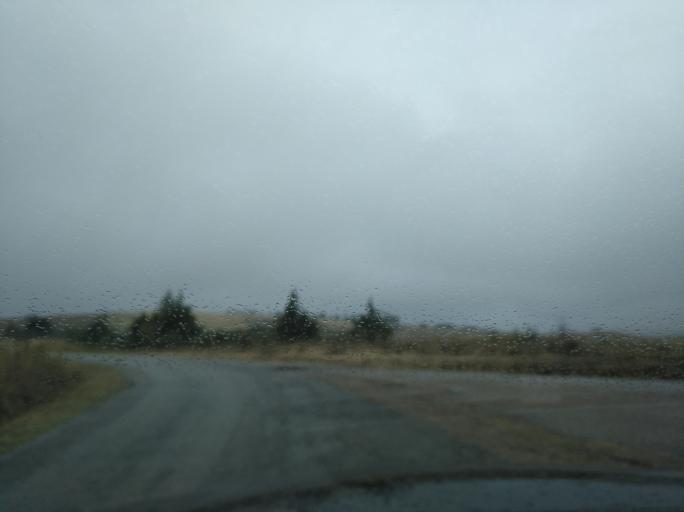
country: PT
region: Portalegre
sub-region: Campo Maior
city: Campo Maior
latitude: 38.9815
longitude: -7.0914
